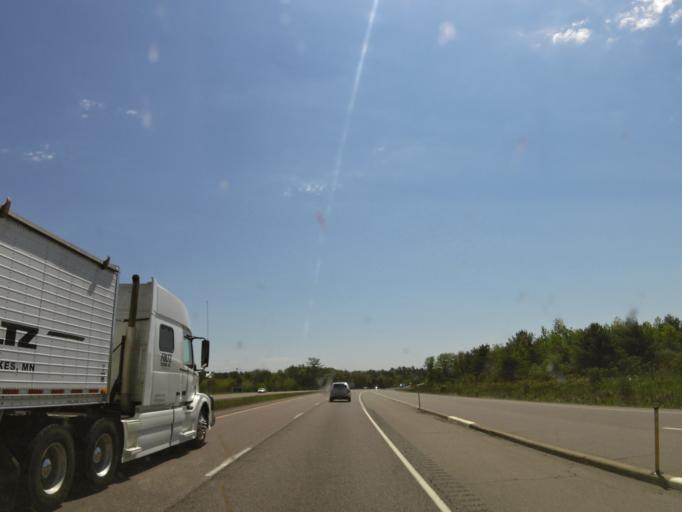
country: US
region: Wisconsin
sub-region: Jackson County
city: Black River Falls
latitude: 44.3087
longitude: -90.8408
